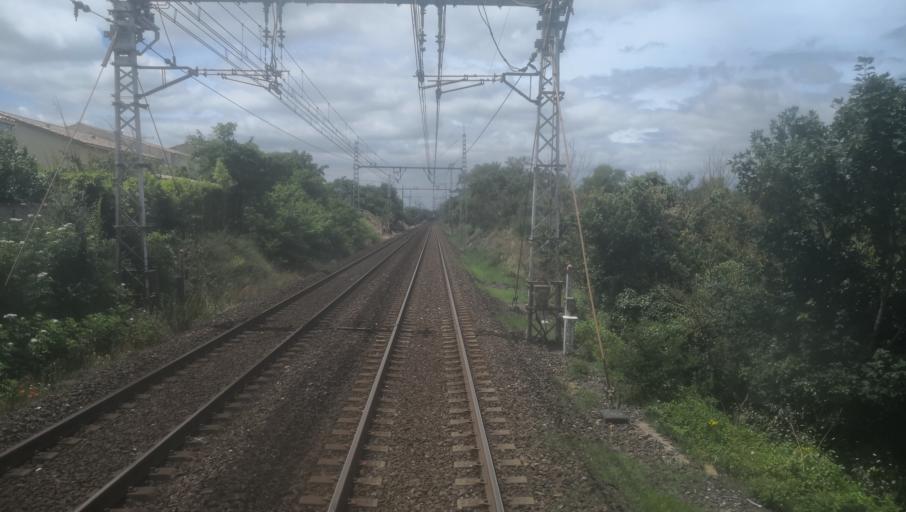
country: FR
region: Languedoc-Roussillon
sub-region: Departement de l'Aude
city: Carcassonne
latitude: 43.2193
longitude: 2.3719
